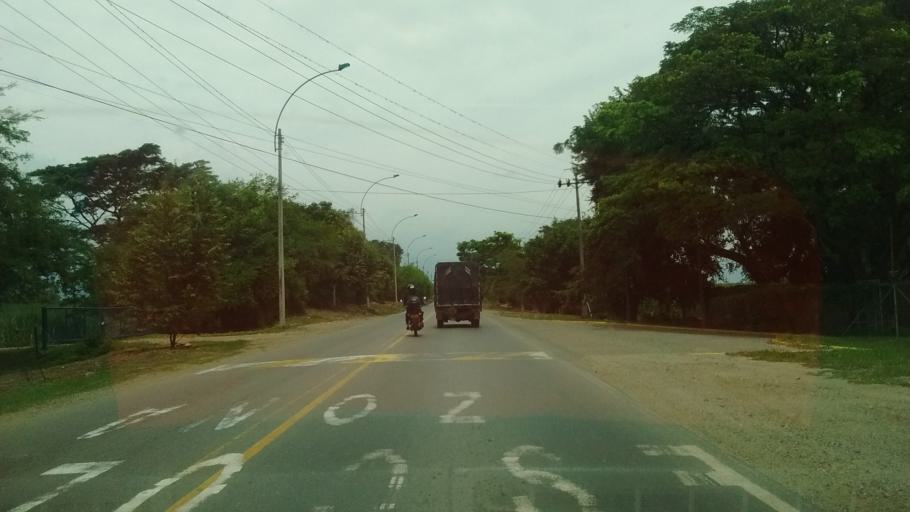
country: CO
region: Valle del Cauca
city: Jamundi
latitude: 3.3221
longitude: -76.4979
